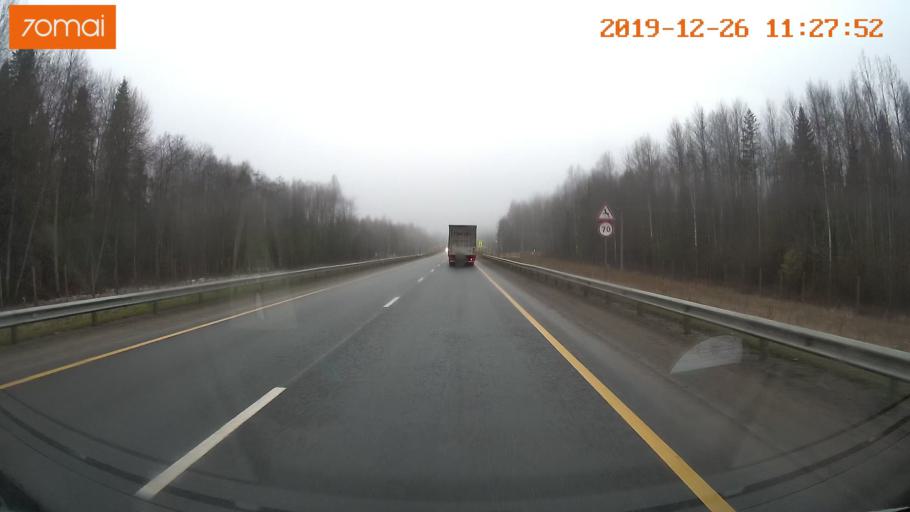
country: RU
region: Vologda
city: Chebsara
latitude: 59.1532
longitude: 38.8267
